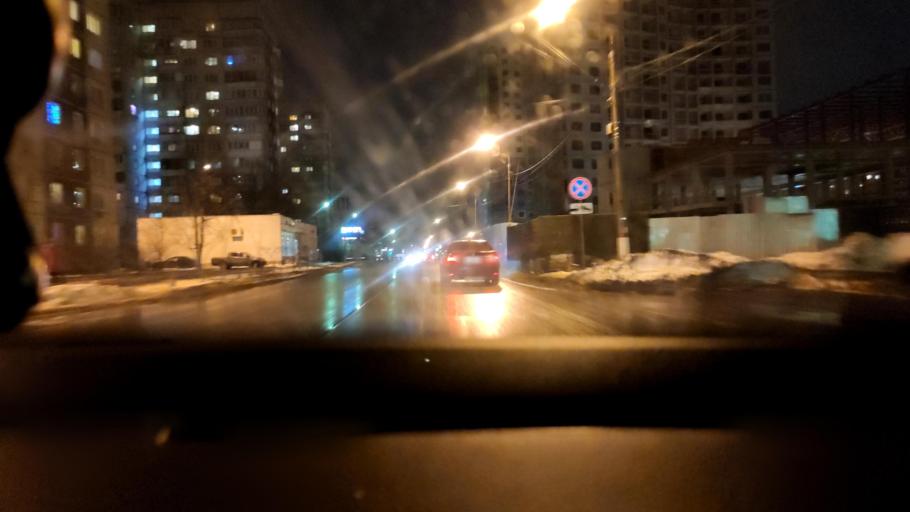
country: RU
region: Moskovskaya
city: Bykovo
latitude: 55.6049
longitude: 38.0778
